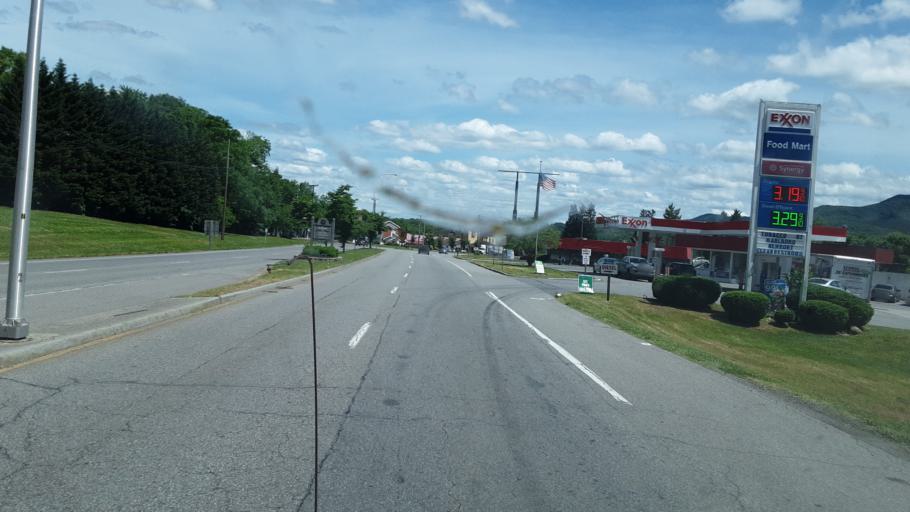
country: US
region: Virginia
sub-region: City of Salem
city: Salem
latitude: 37.2924
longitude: -80.0983
